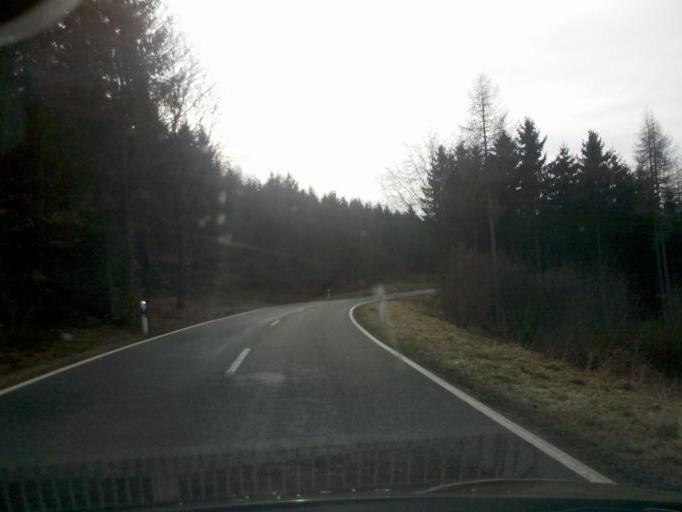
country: DE
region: Hesse
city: Dillenburg
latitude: 50.7884
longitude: 8.2812
